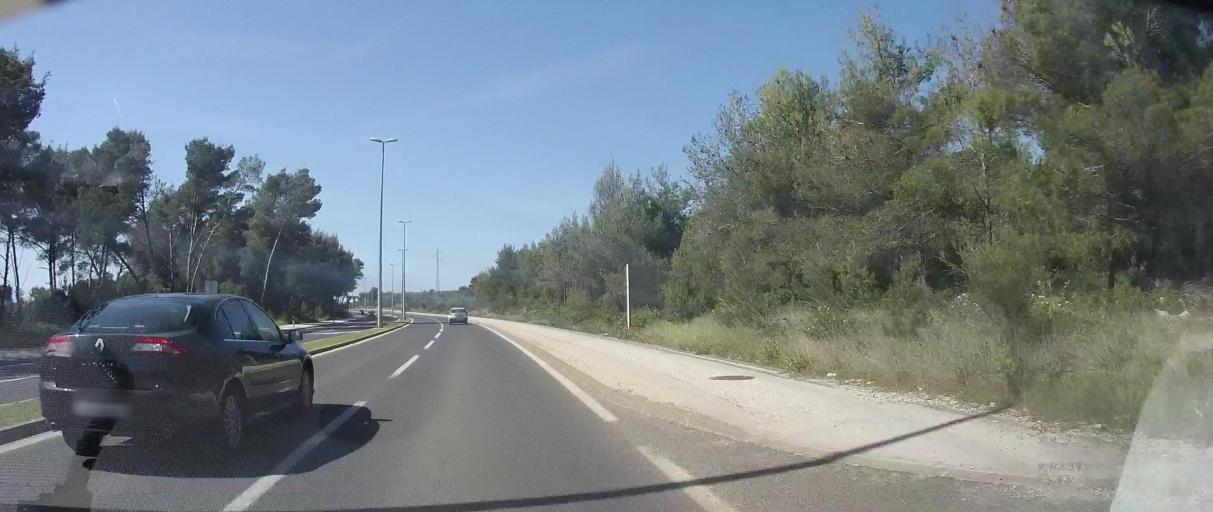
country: HR
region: Zadarska
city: Bibinje
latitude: 44.0864
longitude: 15.2832
